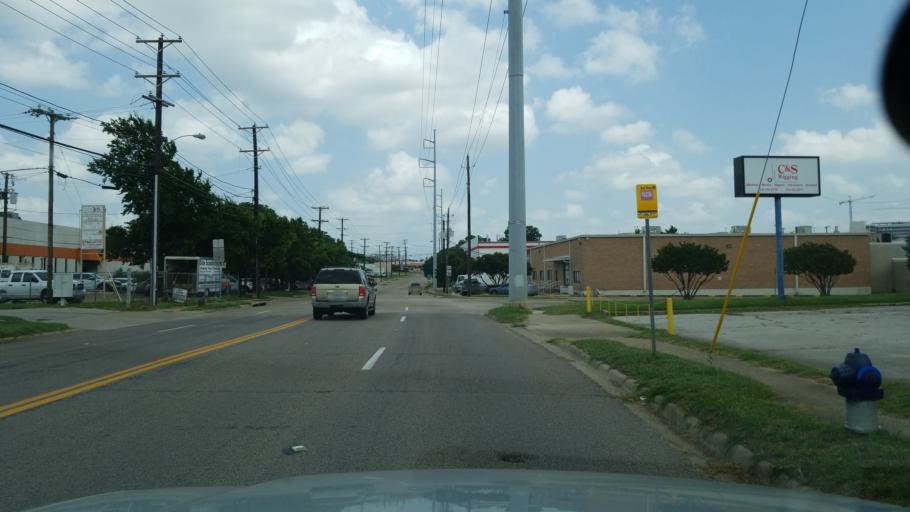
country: US
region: Texas
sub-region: Dallas County
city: University Park
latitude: 32.8262
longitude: -96.8592
